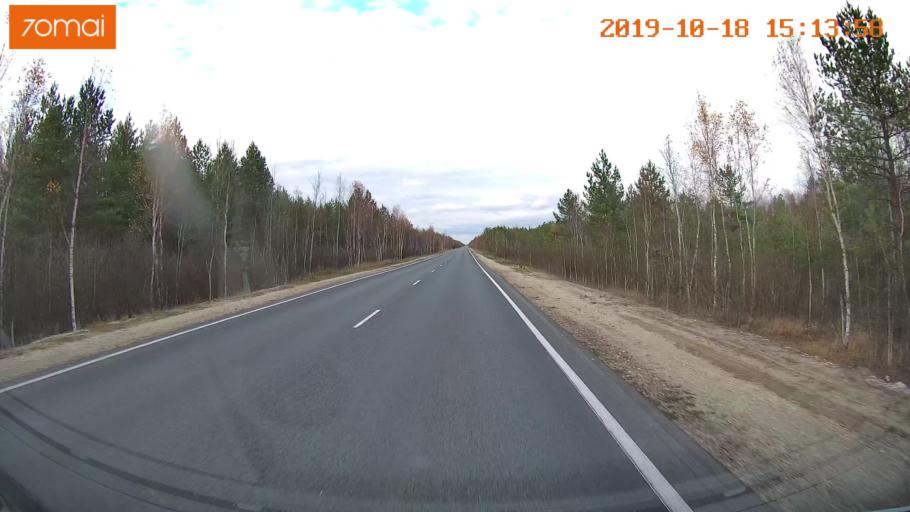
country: RU
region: Vladimir
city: Gus'-Khrustal'nyy
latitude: 55.5951
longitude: 40.7193
